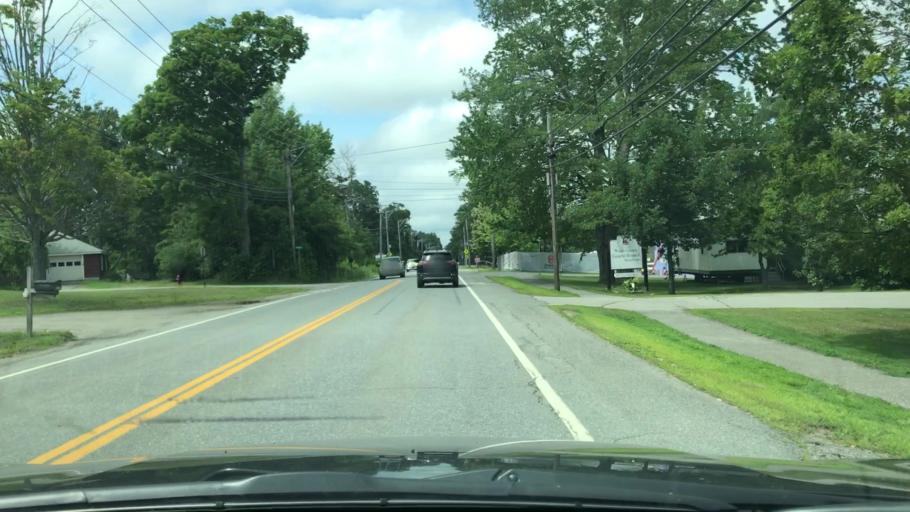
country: US
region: Maine
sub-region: Waldo County
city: Belfast
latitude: 44.4112
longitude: -68.9942
